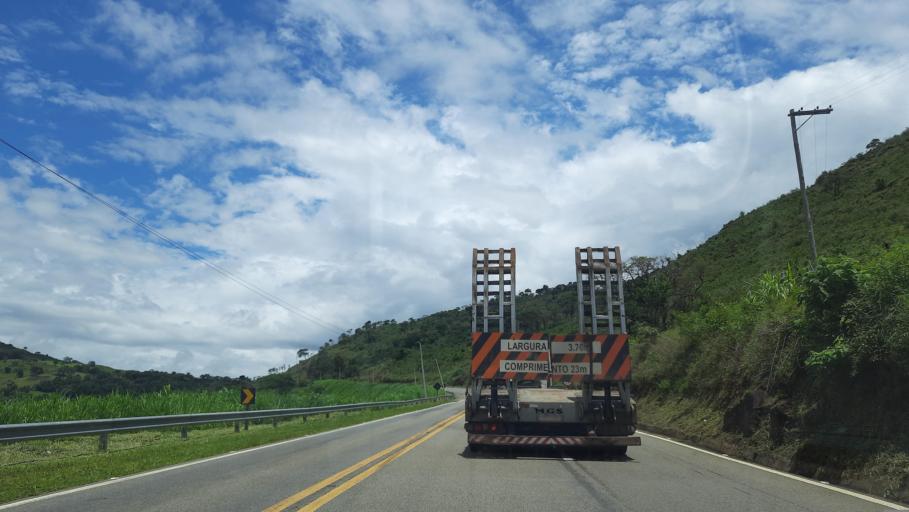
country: BR
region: Sao Paulo
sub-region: Vargem Grande Do Sul
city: Vargem Grande do Sul
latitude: -21.8318
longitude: -46.7625
